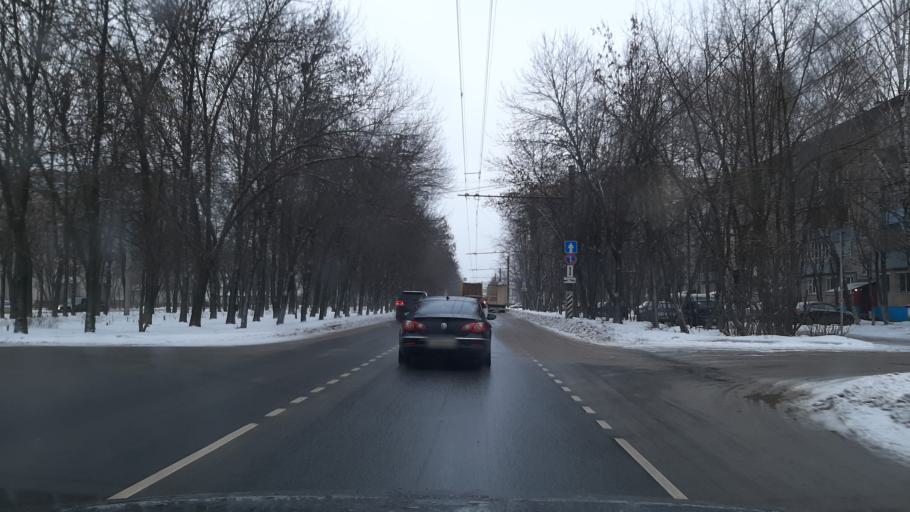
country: RU
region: Ivanovo
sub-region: Gorod Ivanovo
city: Ivanovo
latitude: 56.9629
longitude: 41.0175
